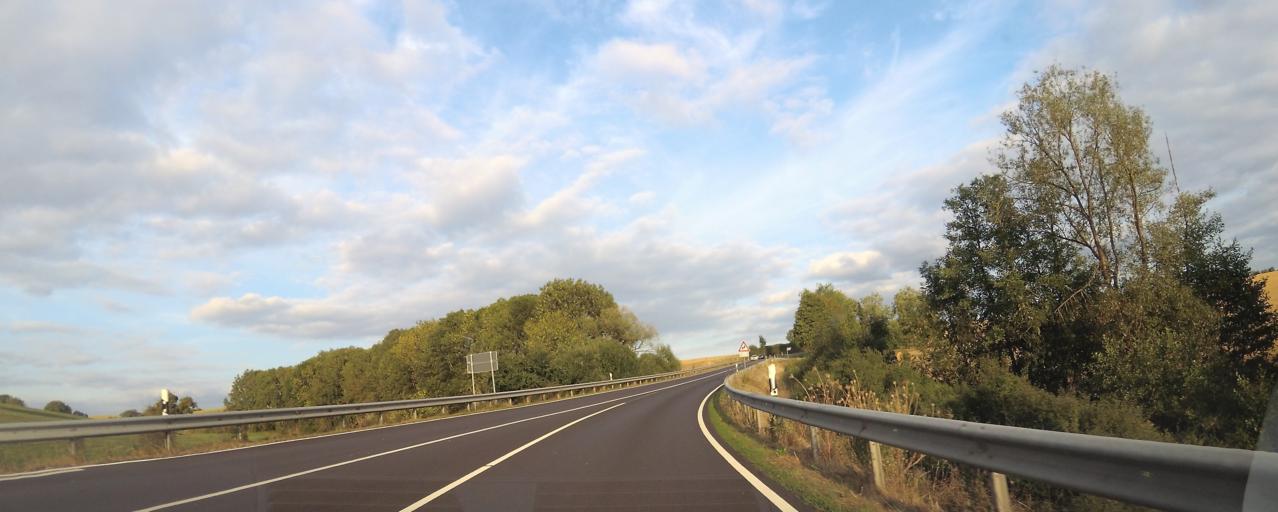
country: DE
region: Rheinland-Pfalz
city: Dudeldorf
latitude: 49.9668
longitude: 6.6486
